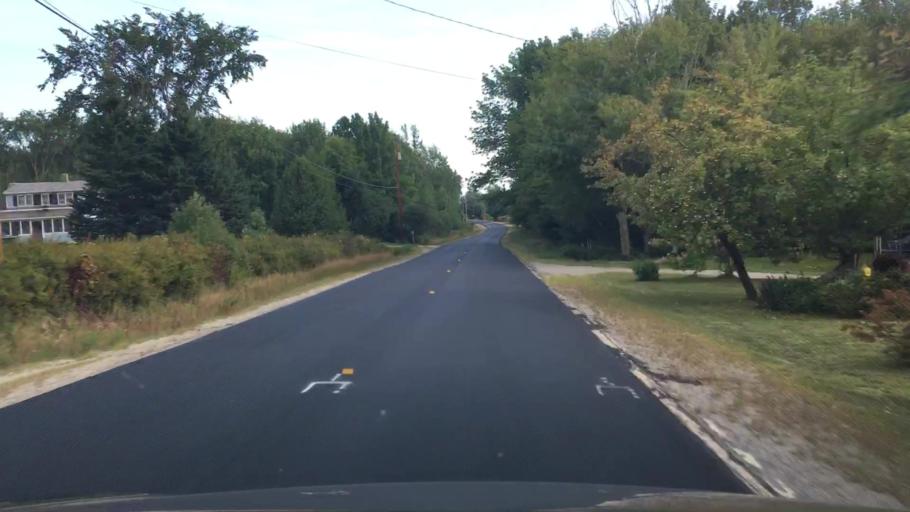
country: US
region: Maine
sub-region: Hancock County
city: Orland
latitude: 44.5508
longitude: -68.6211
